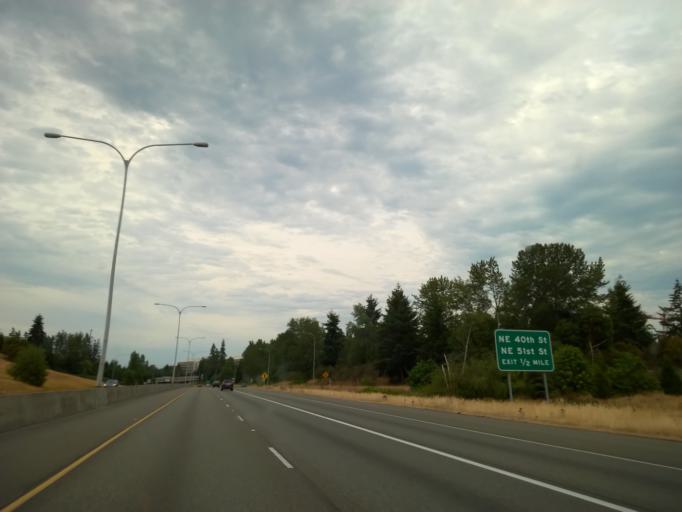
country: US
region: Washington
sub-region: King County
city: Redmond
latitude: 47.6354
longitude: -122.1412
